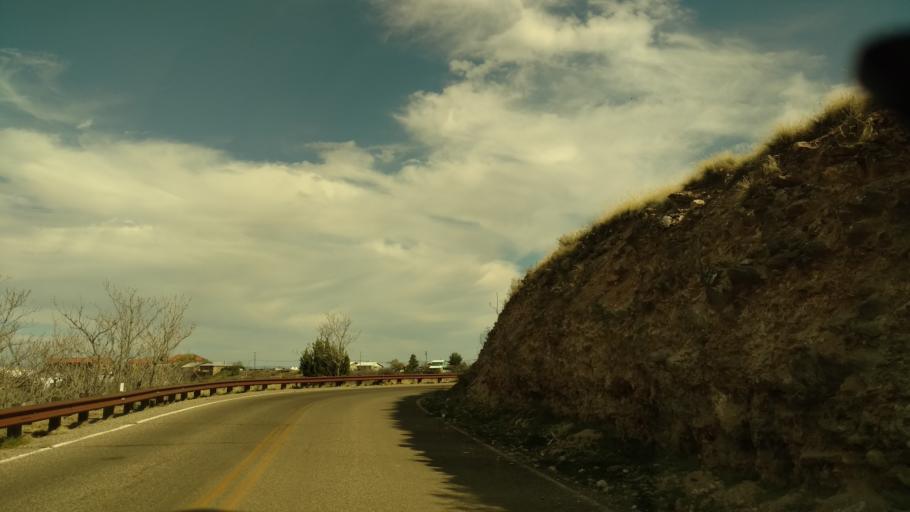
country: US
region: Arizona
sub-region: Yavapai County
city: Clarkdale
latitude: 34.7511
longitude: -112.1121
